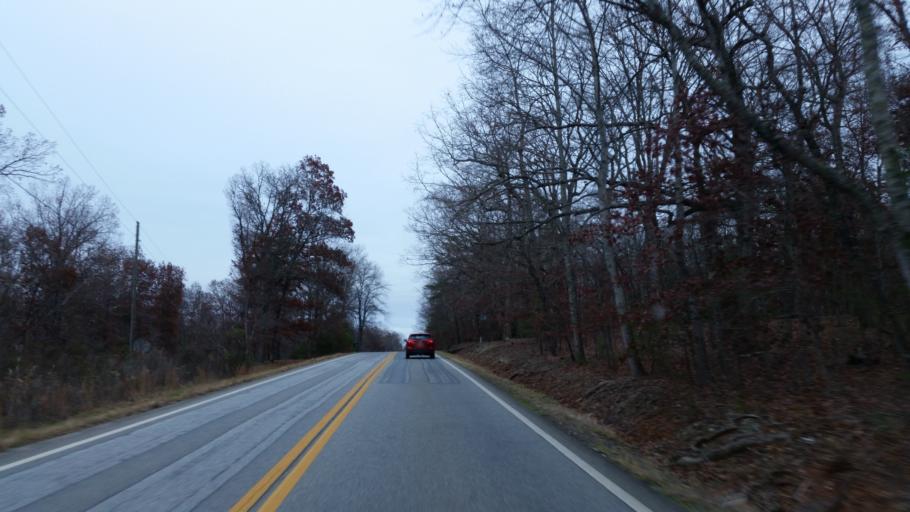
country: US
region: Georgia
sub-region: Dawson County
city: Dawsonville
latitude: 34.4311
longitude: -84.0675
